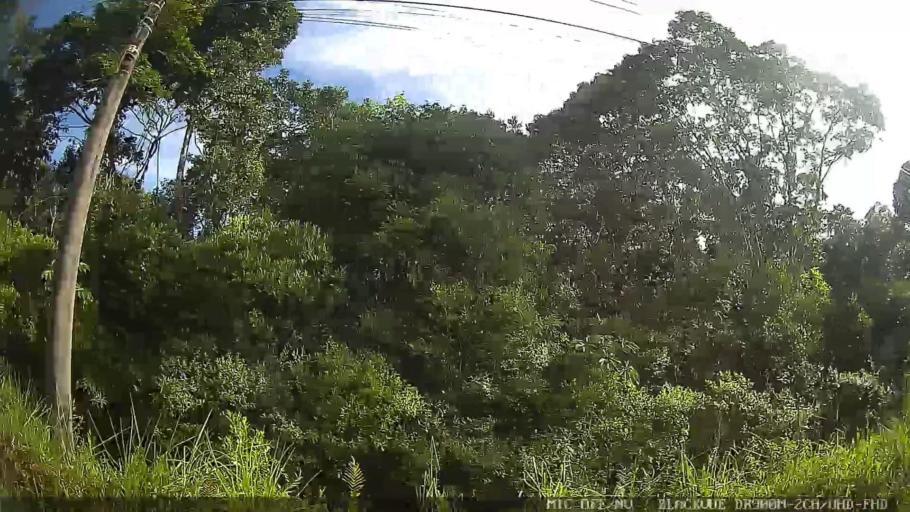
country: BR
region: Sao Paulo
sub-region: Itanhaem
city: Itanhaem
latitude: -24.2033
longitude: -46.8875
